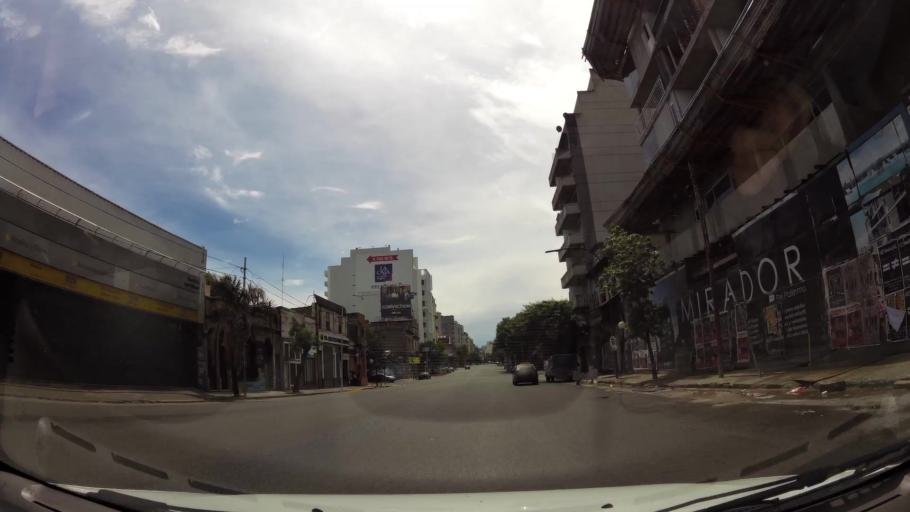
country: AR
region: Buenos Aires F.D.
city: Colegiales
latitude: -34.5884
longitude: -58.4390
